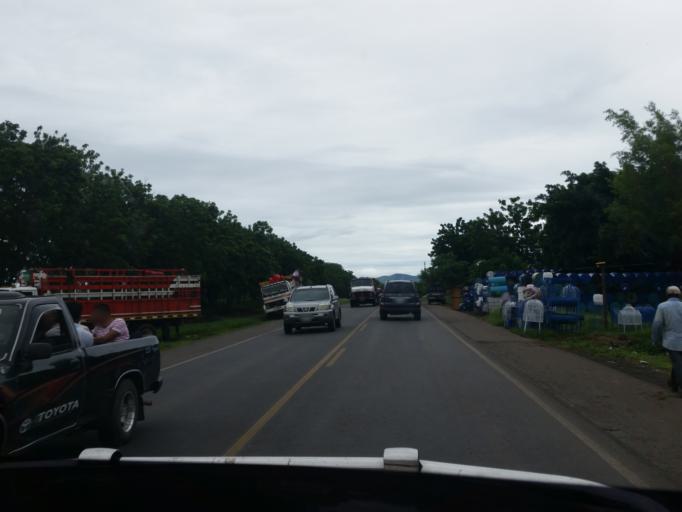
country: NI
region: Managua
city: Tipitapa
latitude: 12.2678
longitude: -86.0757
